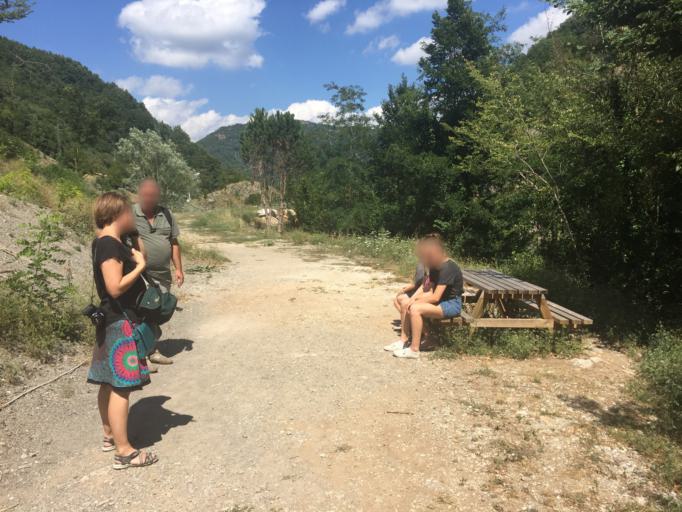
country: IT
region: Tuscany
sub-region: Provincia di Lucca
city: Fontana delle Monache
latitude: 44.1139
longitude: 10.2908
